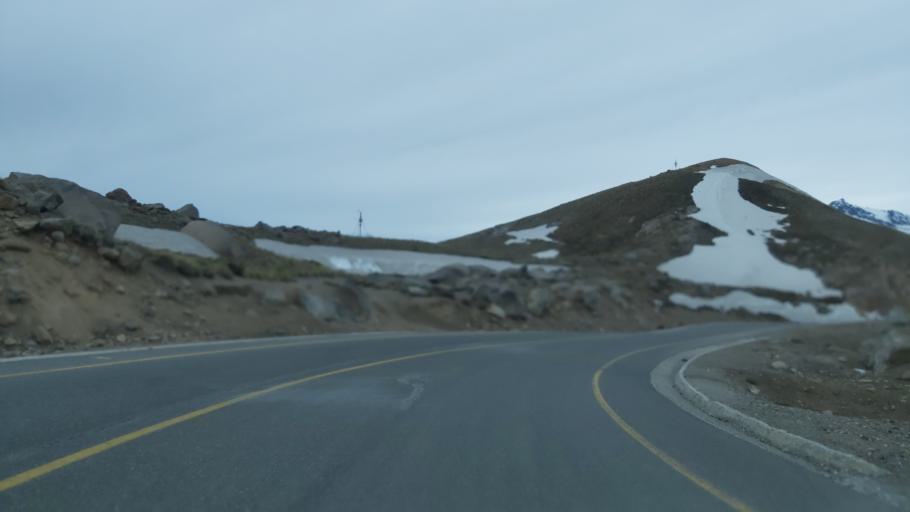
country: CL
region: Maule
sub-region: Provincia de Linares
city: Colbun
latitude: -35.9801
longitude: -70.5650
